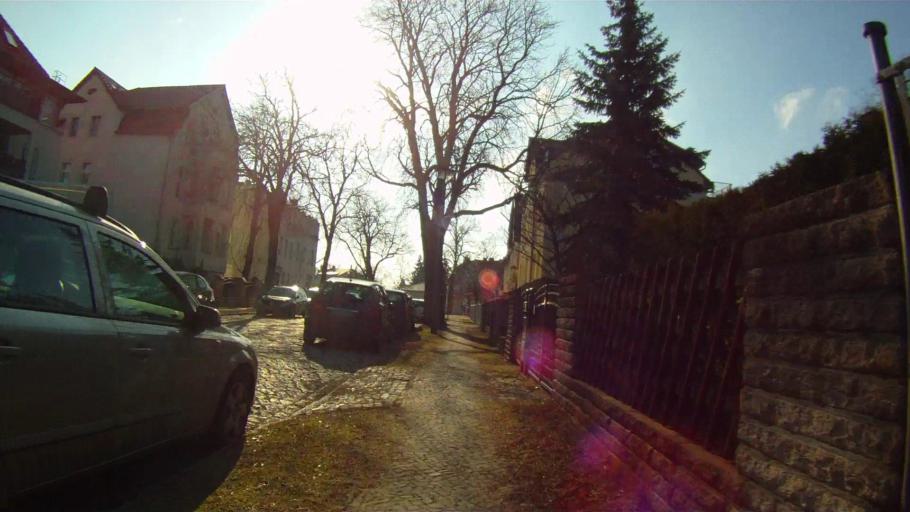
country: DE
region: Berlin
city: Rahnsdorf
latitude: 52.4419
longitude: 13.6891
